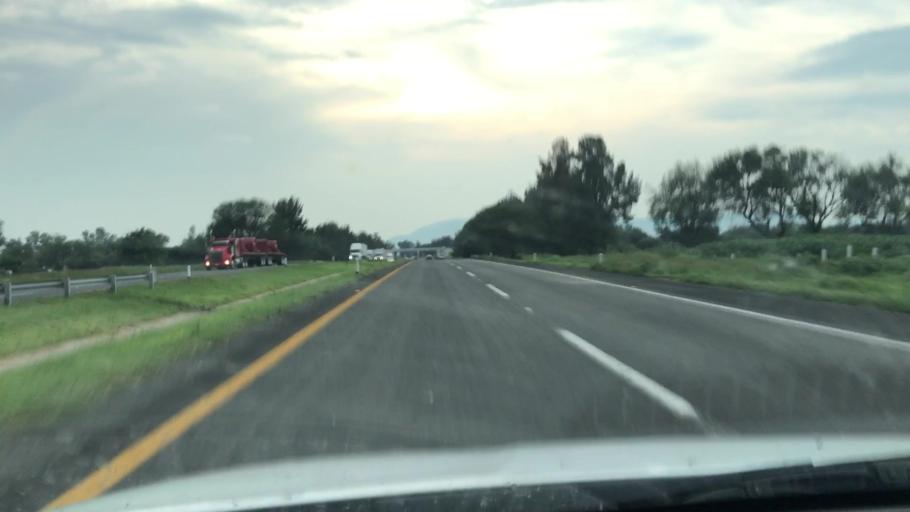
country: MX
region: Michoacan
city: Vistahermosa de Negrete
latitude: 20.3175
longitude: -102.5005
